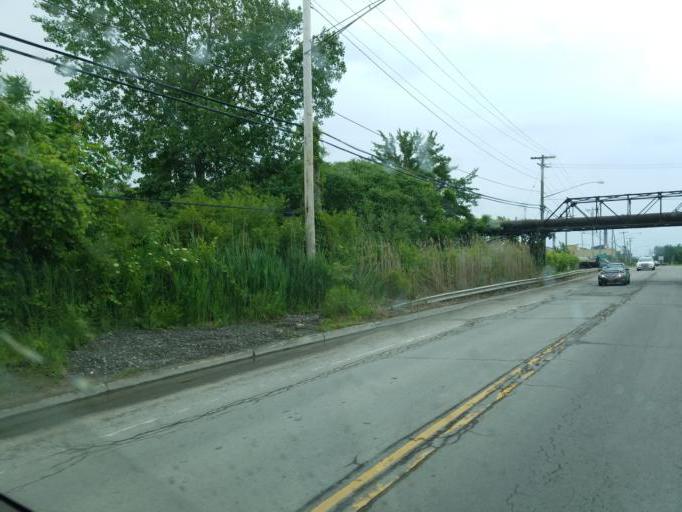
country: US
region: New York
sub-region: Erie County
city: Grandyle Village
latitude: 42.9851
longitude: -78.9358
